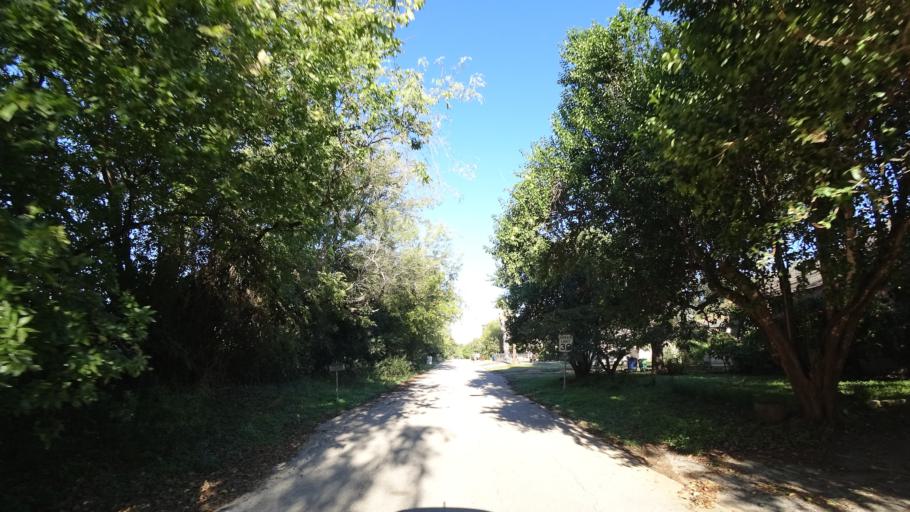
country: US
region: Texas
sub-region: Travis County
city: Hornsby Bend
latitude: 30.2065
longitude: -97.6426
